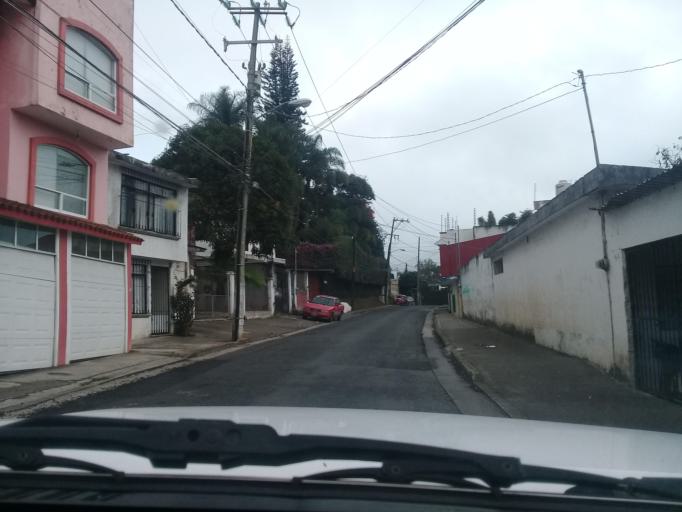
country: MX
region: Veracruz
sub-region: Xalapa
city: Xalapa de Enriquez
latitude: 19.5140
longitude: -96.9113
